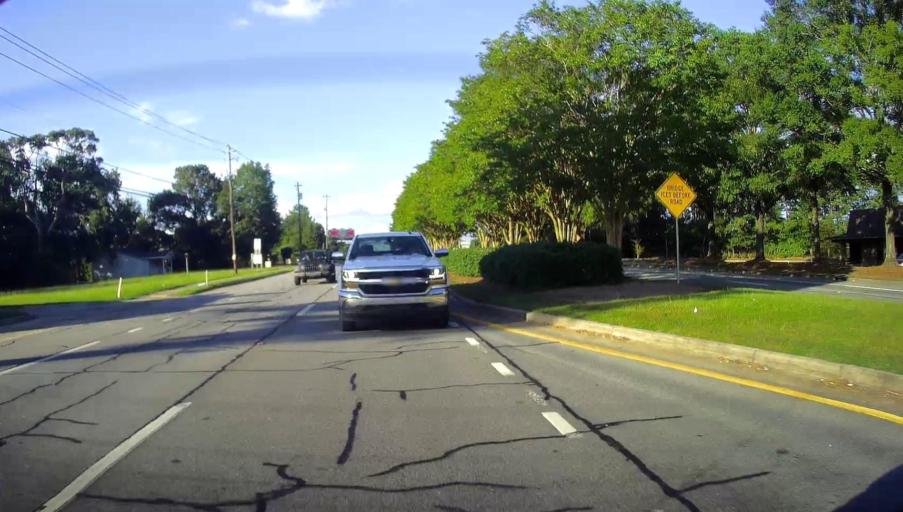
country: US
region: Alabama
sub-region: Russell County
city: Phenix City
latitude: 32.5269
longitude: -84.9608
